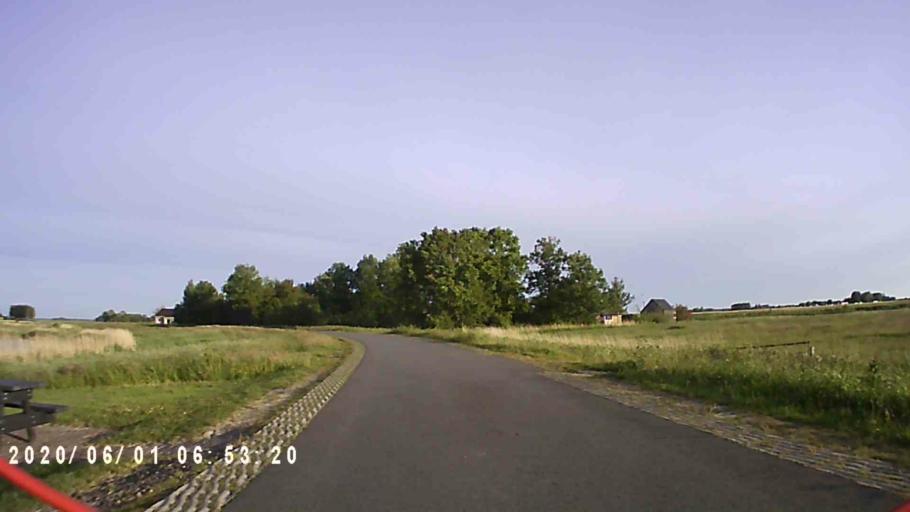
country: NL
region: Friesland
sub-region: Gemeente Kollumerland en Nieuwkruisland
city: Kollum
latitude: 53.3115
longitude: 6.1293
